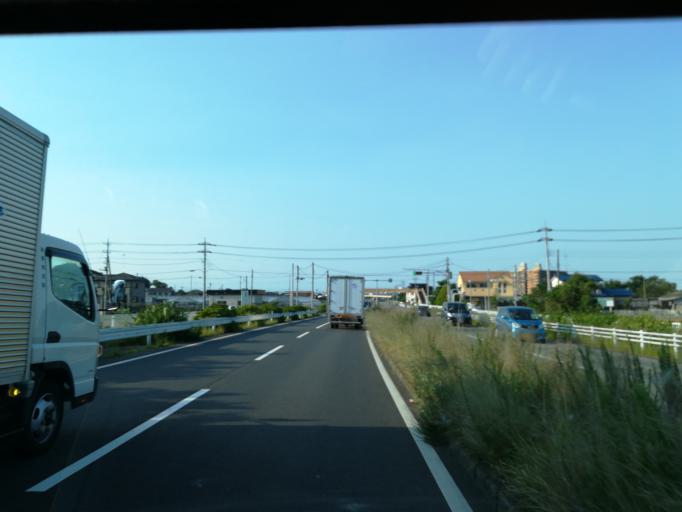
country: JP
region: Saitama
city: Kumagaya
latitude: 36.1199
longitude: 139.3686
